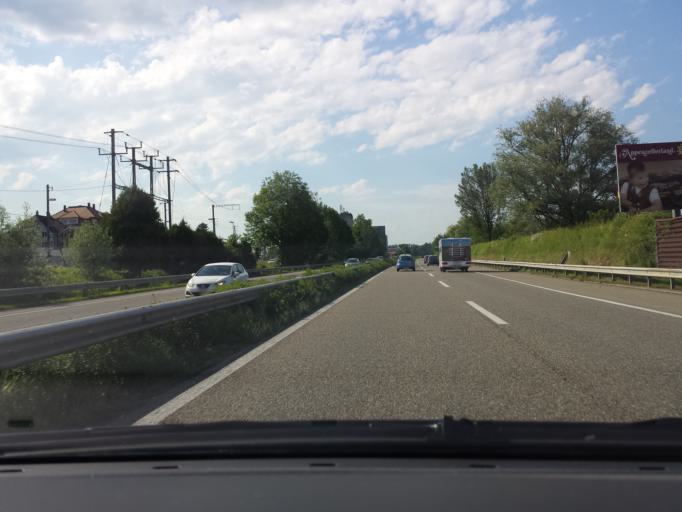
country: CH
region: Saint Gallen
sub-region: Wahlkreis Rheintal
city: Rheineck
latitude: 47.4678
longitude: 9.5911
